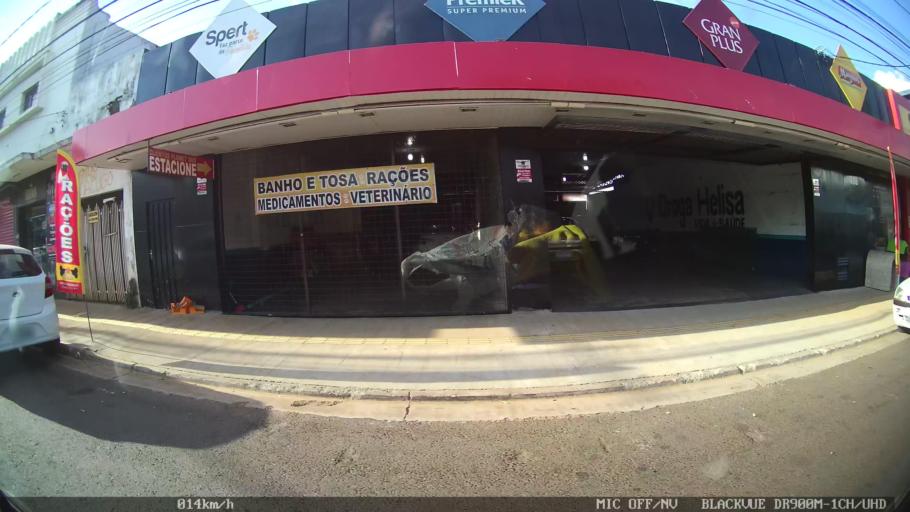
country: BR
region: Sao Paulo
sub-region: Ribeirao Preto
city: Ribeirao Preto
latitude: -21.1579
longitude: -47.8168
